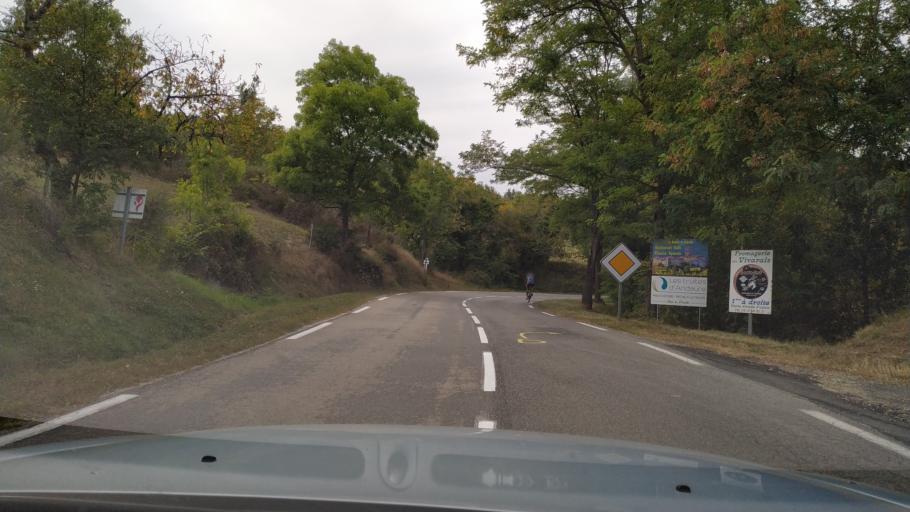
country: FR
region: Rhone-Alpes
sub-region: Departement de l'Ardeche
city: Desaignes
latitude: 44.9969
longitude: 4.5118
